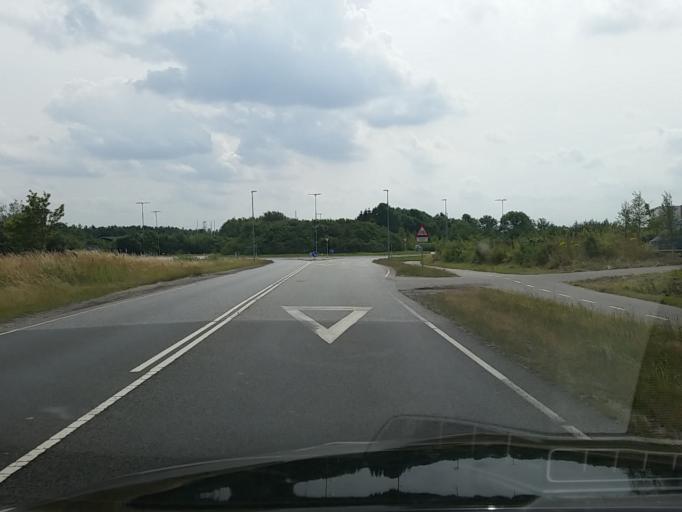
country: DK
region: South Denmark
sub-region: Kolding Kommune
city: Kolding
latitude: 55.5457
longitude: 9.4777
